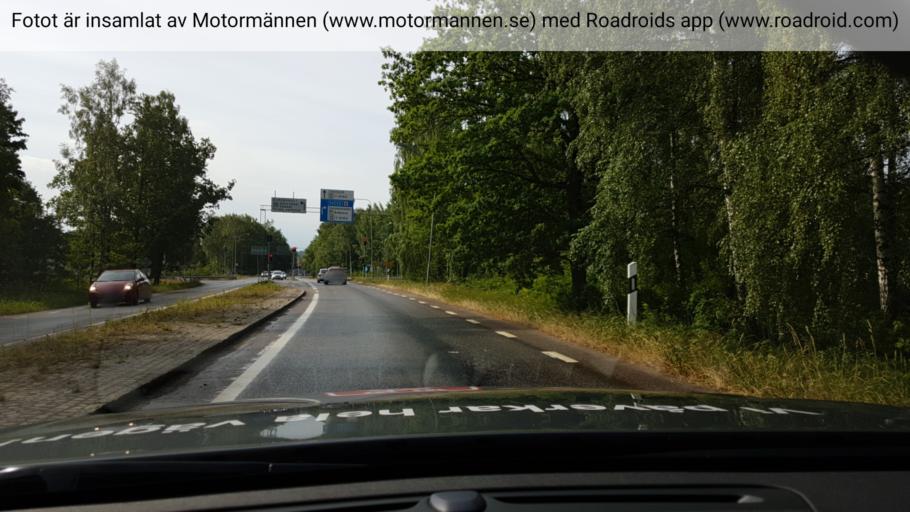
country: SE
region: OEstergoetland
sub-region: Motala Kommun
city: Motala
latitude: 58.5572
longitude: 15.0623
